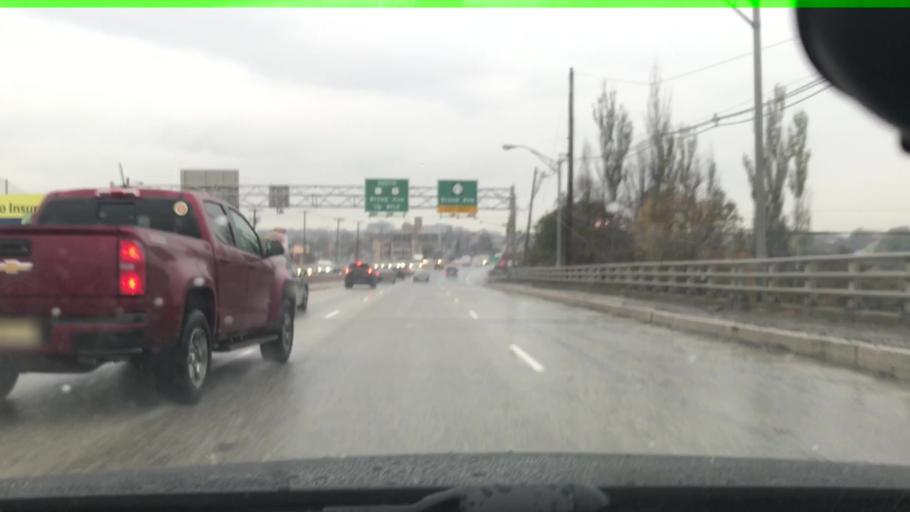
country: US
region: New Jersey
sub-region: Bergen County
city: Ridgefield
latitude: 40.8444
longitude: -74.0111
